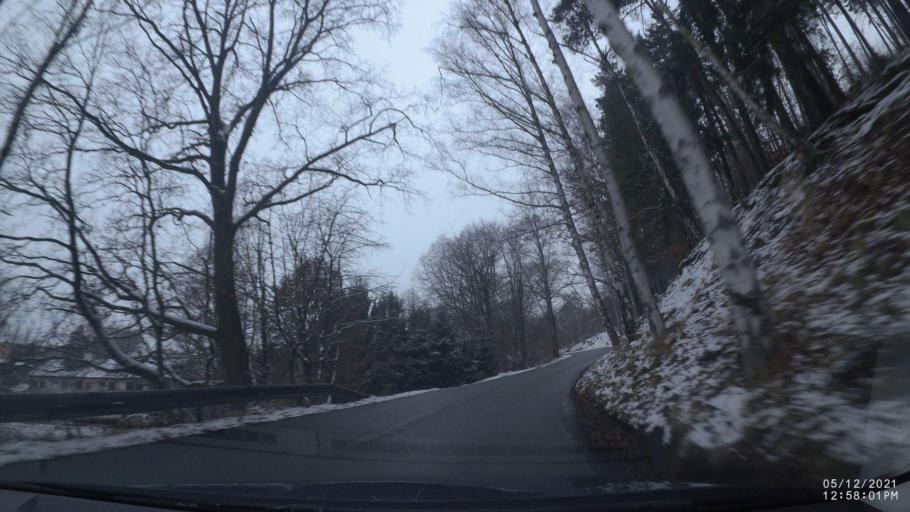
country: CZ
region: Kralovehradecky
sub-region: Okres Nachod
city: Nachod
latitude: 50.4144
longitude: 16.1517
